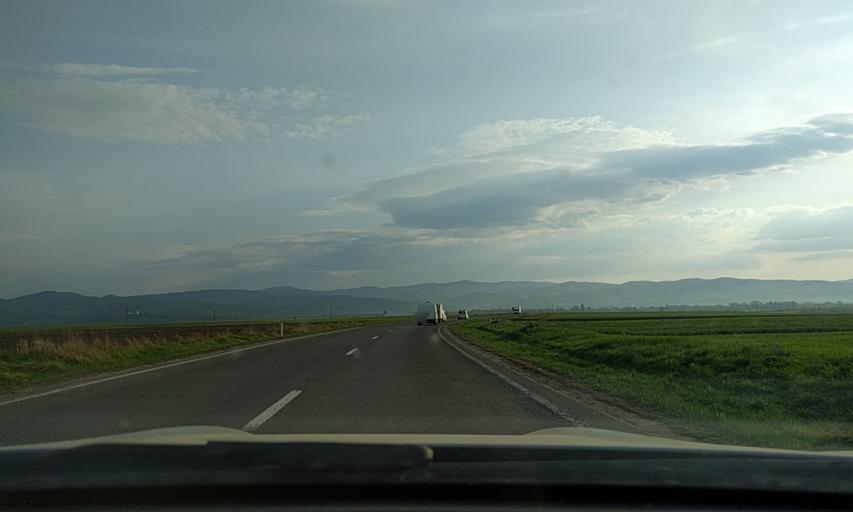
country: RO
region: Covasna
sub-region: Municipiul Targu Secuiesc
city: Lunga
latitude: 46.0337
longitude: 26.2396
